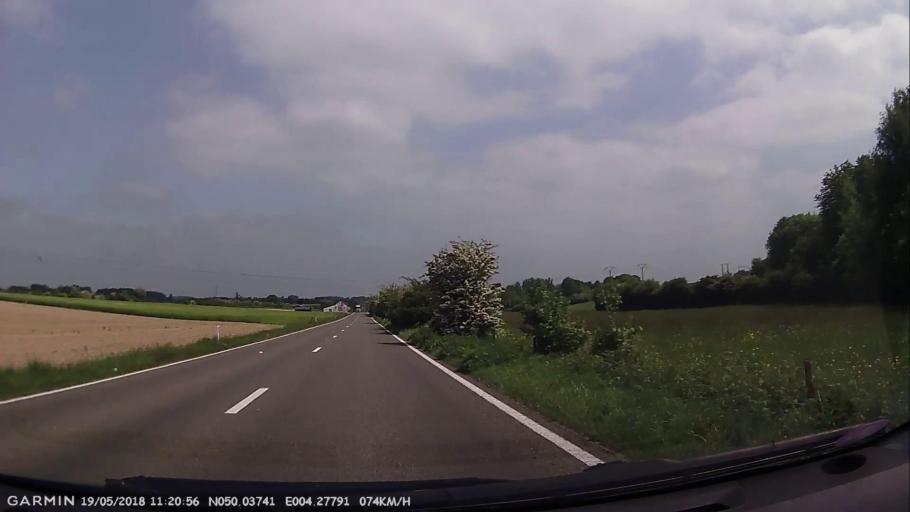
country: BE
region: Wallonia
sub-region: Province du Hainaut
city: Chimay
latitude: 50.0376
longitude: 4.2782
